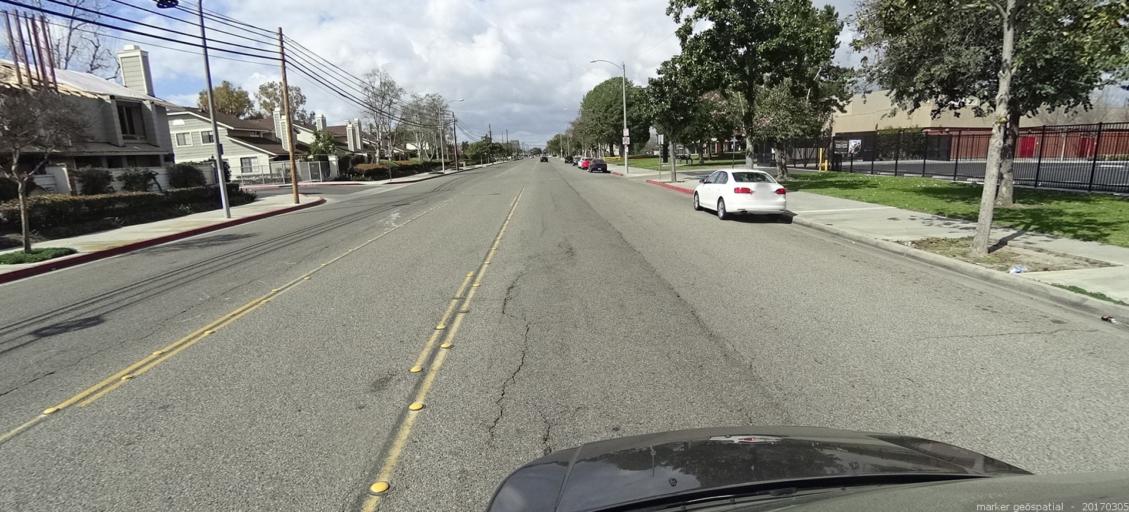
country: US
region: California
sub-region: Orange County
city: Garden Grove
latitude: 33.8106
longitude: -117.9433
